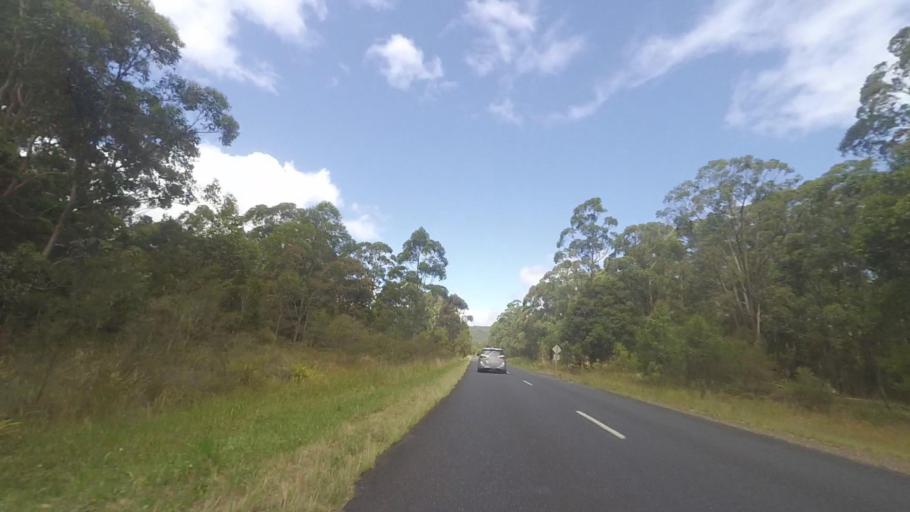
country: AU
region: New South Wales
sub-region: Great Lakes
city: Bulahdelah
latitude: -32.4019
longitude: 152.2627
